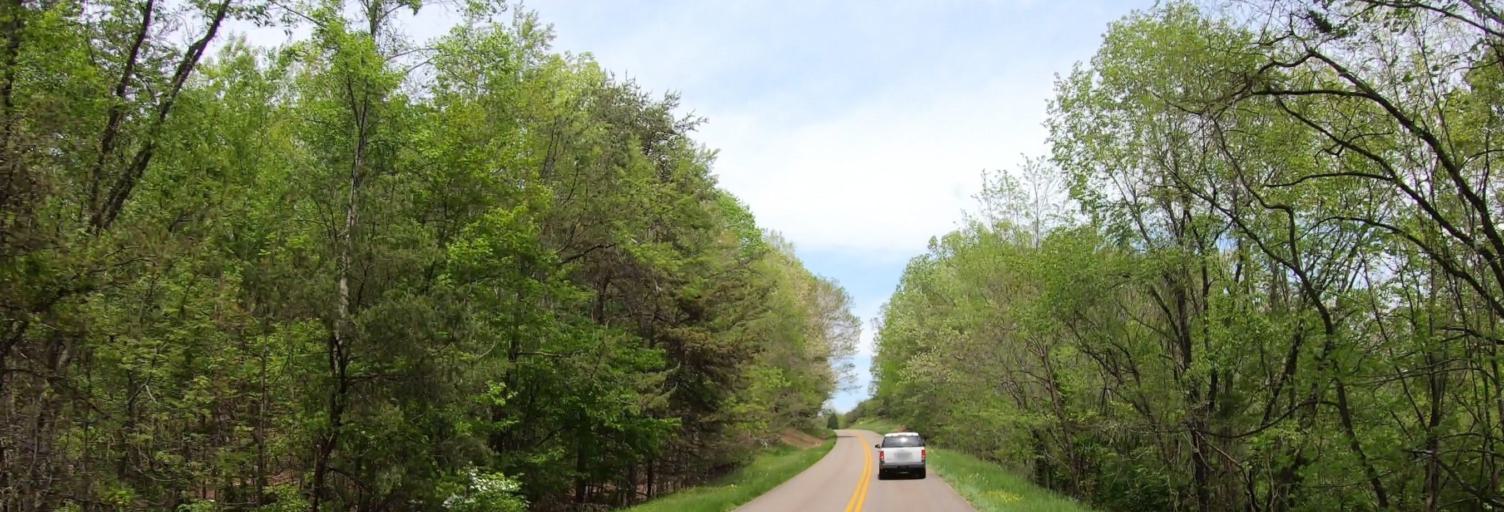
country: US
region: Virginia
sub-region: City of Roanoke
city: Cedar Bluff
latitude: 37.2273
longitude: -79.9095
